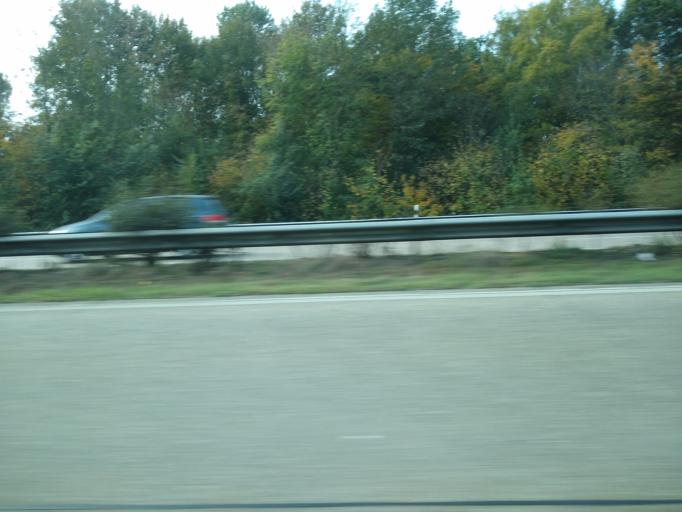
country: DE
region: Lower Saxony
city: Oldenburg
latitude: 53.1389
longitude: 8.2764
